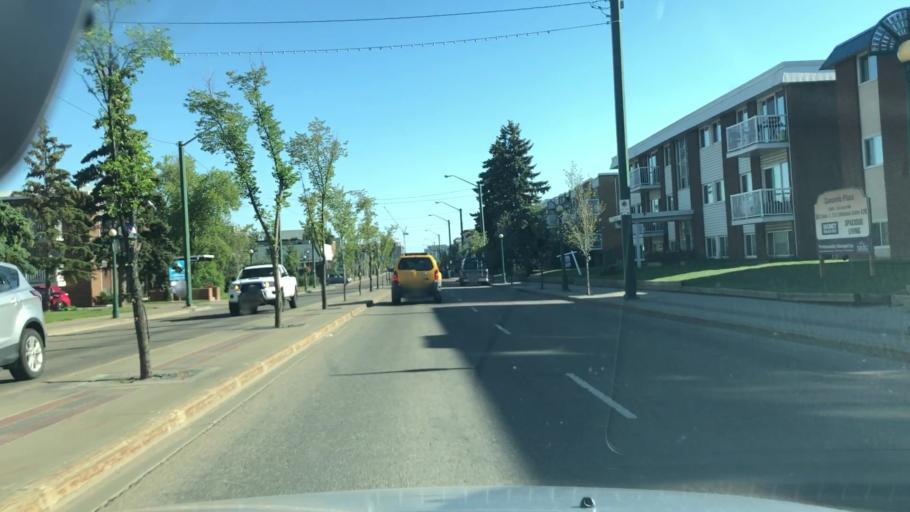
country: CA
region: Alberta
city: Edmonton
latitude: 53.5550
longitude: -113.5360
